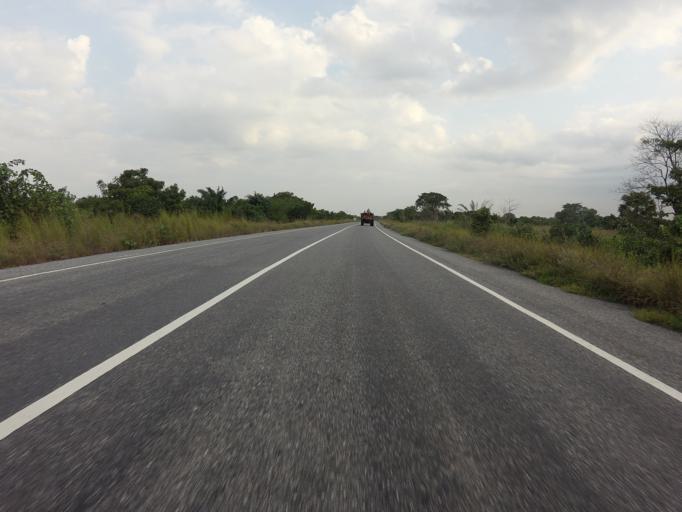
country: GH
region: Volta
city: Ho
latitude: 6.3619
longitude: 0.5361
